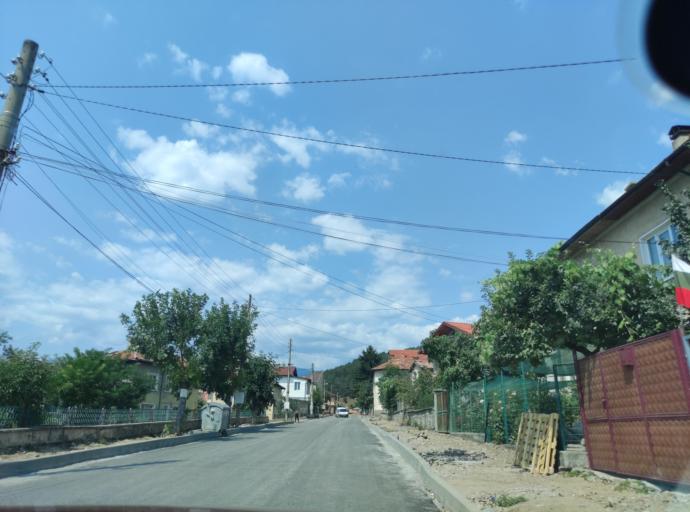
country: BG
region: Blagoevgrad
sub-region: Obshtina Belitsa
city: Belitsa
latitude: 41.9466
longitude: 23.5637
